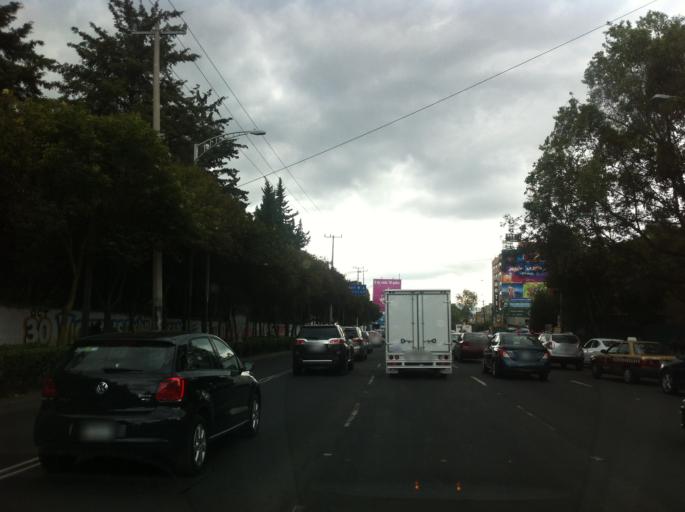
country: MX
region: Mexico City
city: Benito Juarez
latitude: 19.4066
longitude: -99.1538
